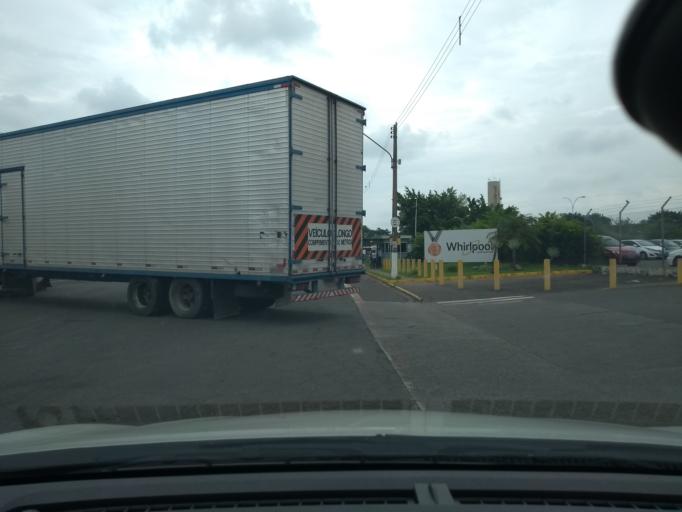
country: BR
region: Sao Paulo
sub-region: Rio Claro
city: Rio Claro
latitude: -22.3771
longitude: -47.5459
